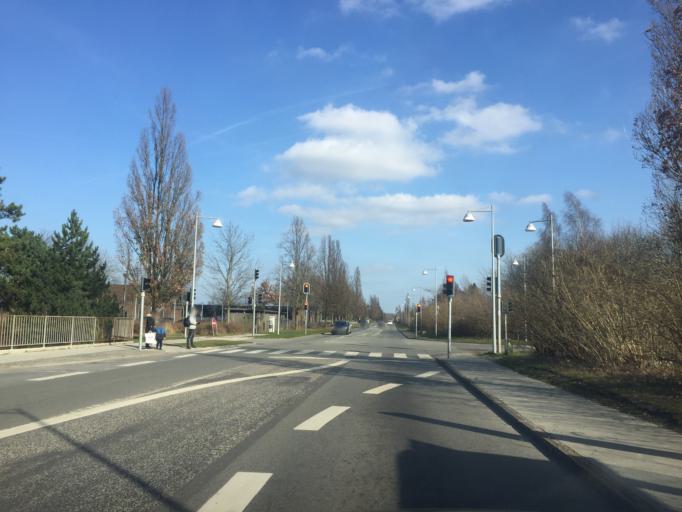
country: DK
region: Capital Region
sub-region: Albertslund Kommune
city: Albertslund
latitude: 55.6749
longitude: 12.3616
